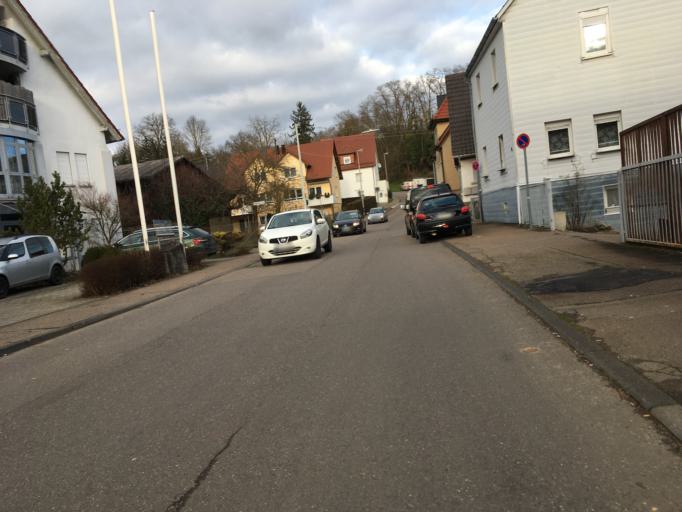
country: DE
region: Baden-Wuerttemberg
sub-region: Regierungsbezirk Stuttgart
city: Bad Wimpfen
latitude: 49.1949
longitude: 9.1428
